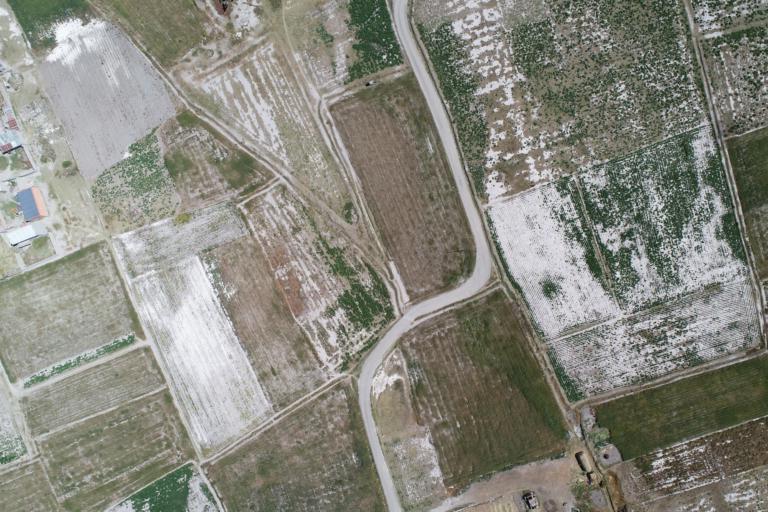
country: BO
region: La Paz
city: Achacachi
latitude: -16.0147
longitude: -68.7237
